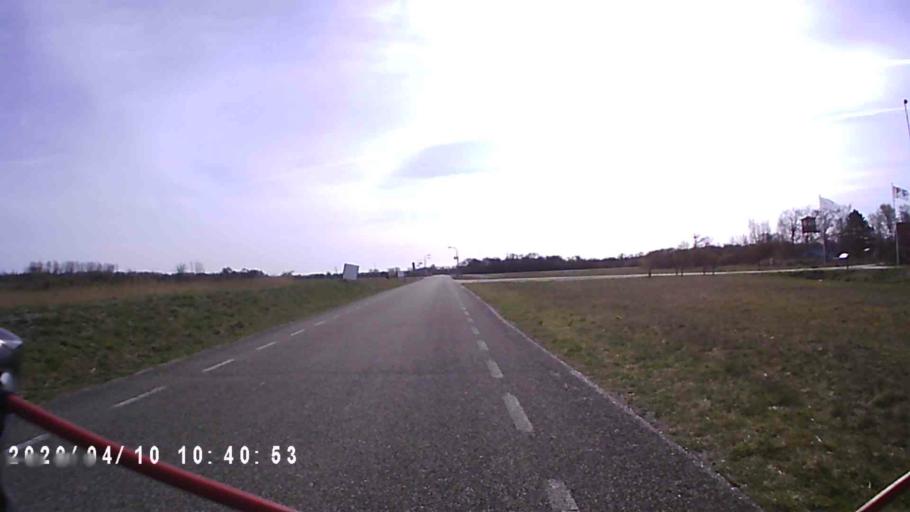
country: NL
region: Groningen
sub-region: Gemeente De Marne
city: Ulrum
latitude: 53.3862
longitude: 6.2347
